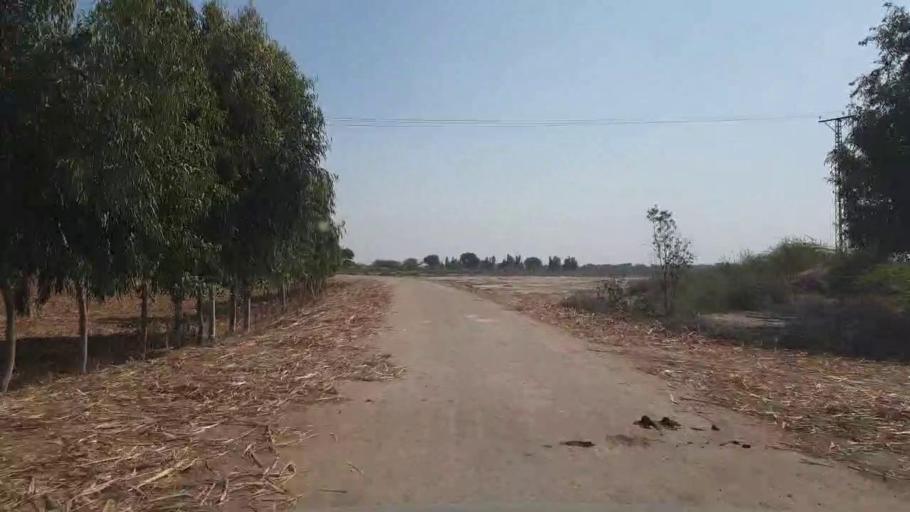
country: PK
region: Sindh
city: Digri
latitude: 25.0947
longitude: 69.2492
